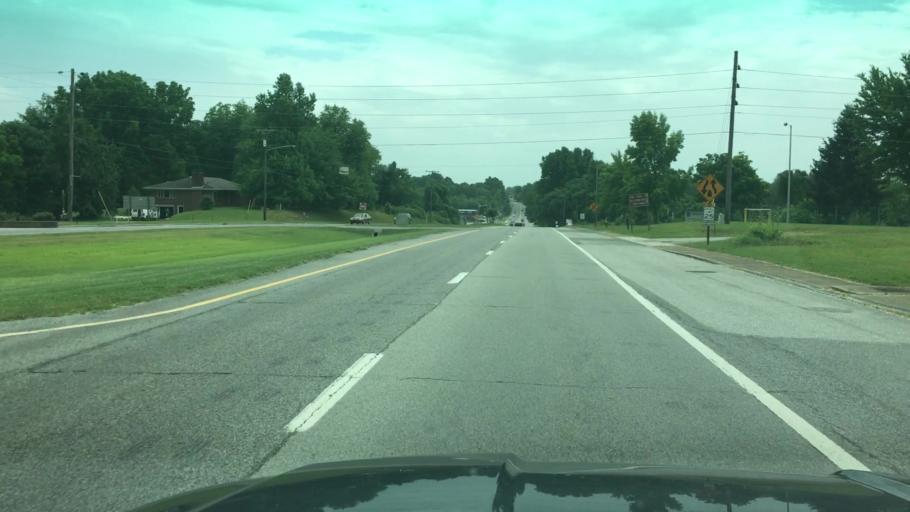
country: US
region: Tennessee
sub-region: Coffee County
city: Manchester
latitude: 35.4870
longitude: -86.0758
